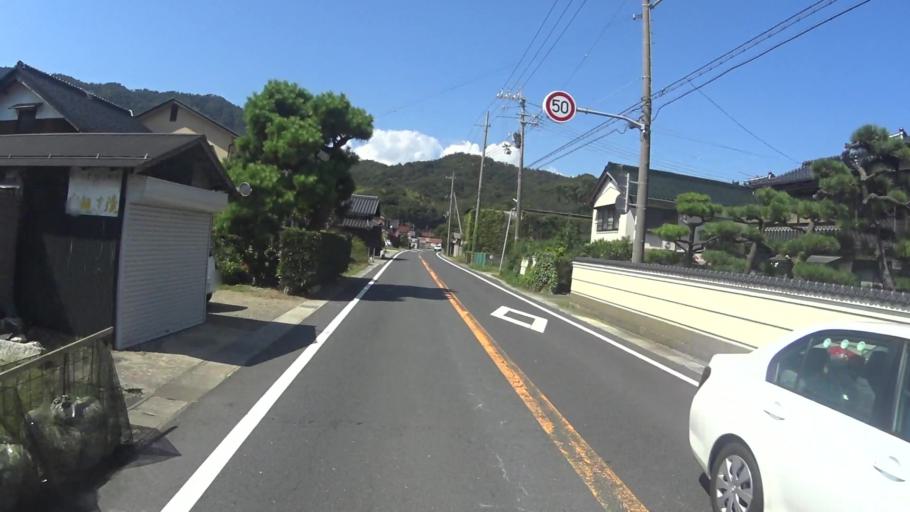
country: JP
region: Kyoto
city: Maizuru
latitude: 35.5215
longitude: 135.2762
